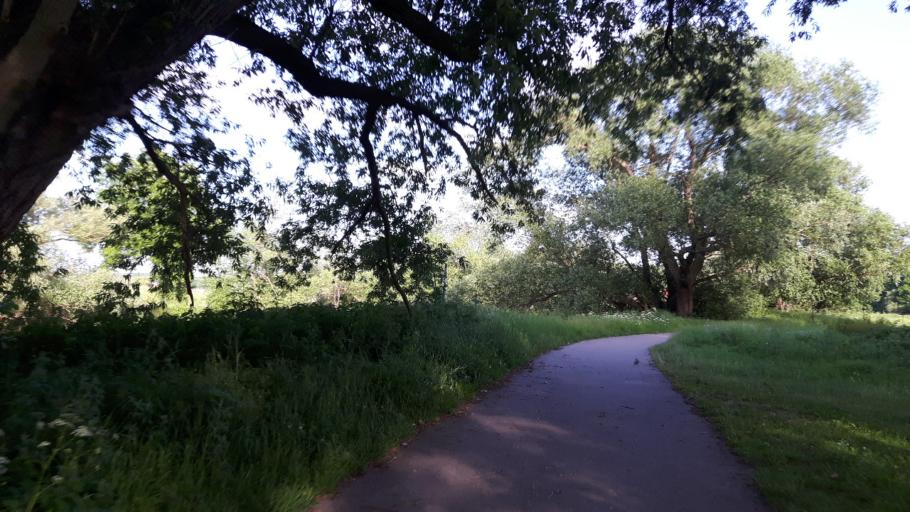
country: DE
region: Saxony-Anhalt
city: Naumburg
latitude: 51.1561
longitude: 11.8361
